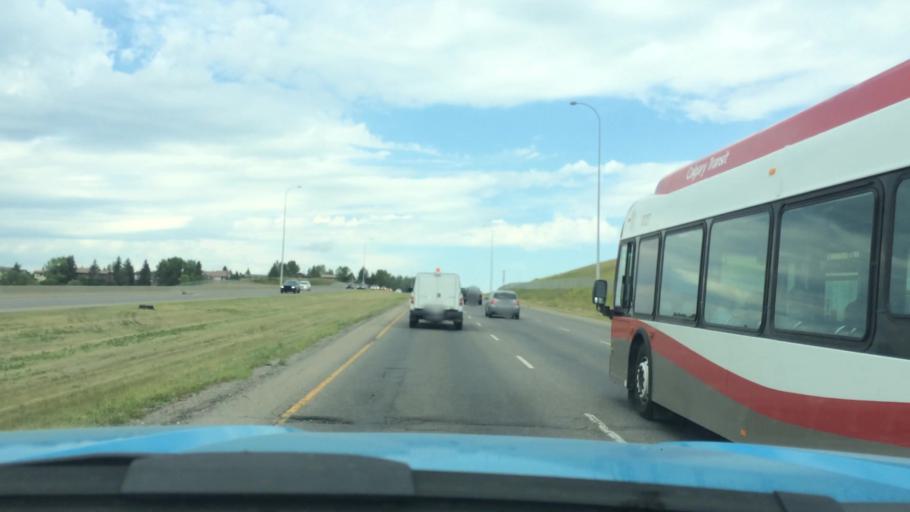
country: CA
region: Alberta
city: Calgary
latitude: 51.1197
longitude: -114.1340
